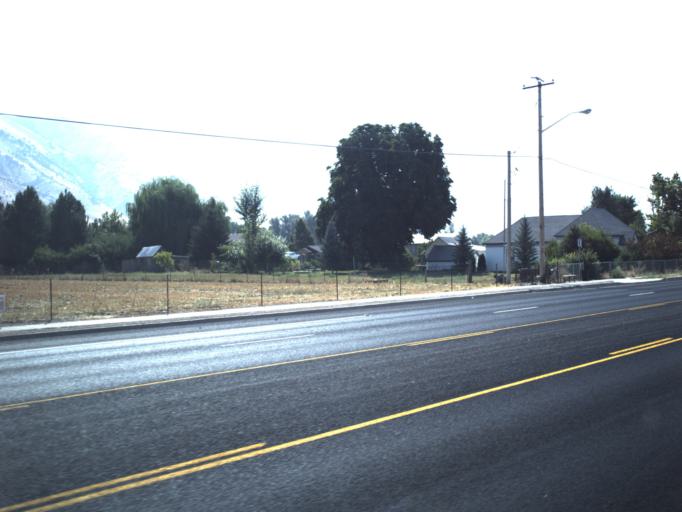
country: US
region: Utah
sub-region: Cache County
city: Nibley
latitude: 41.6646
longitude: -111.8338
